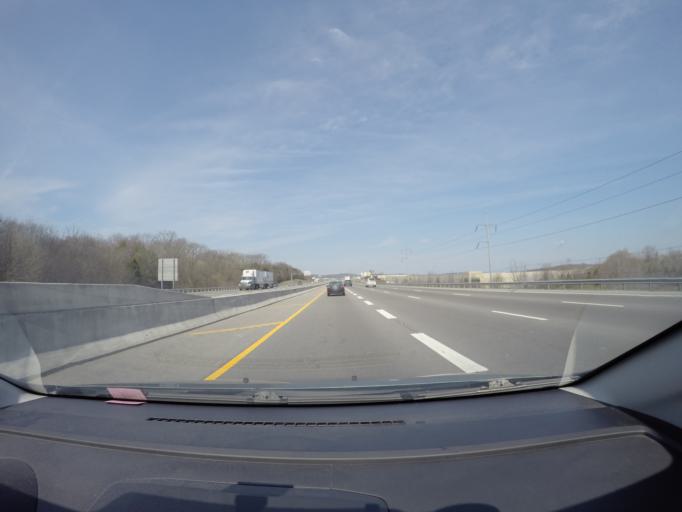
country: US
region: Tennessee
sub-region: Rutherford County
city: La Vergne
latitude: 35.9870
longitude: -86.5835
